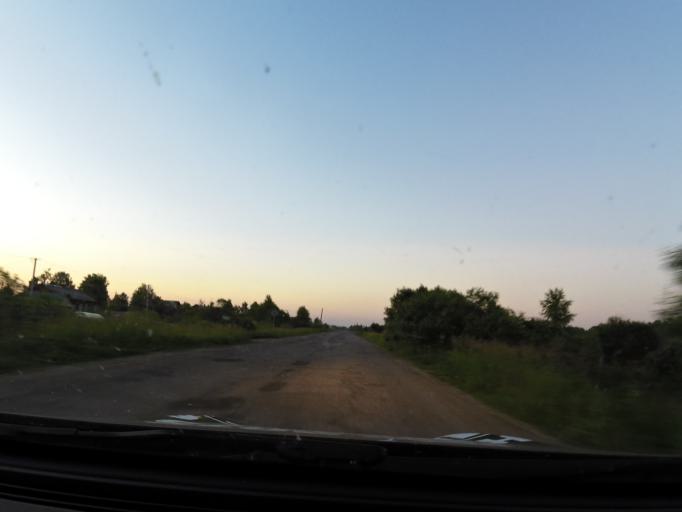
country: RU
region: Kostroma
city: Buy
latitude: 58.4666
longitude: 41.4145
